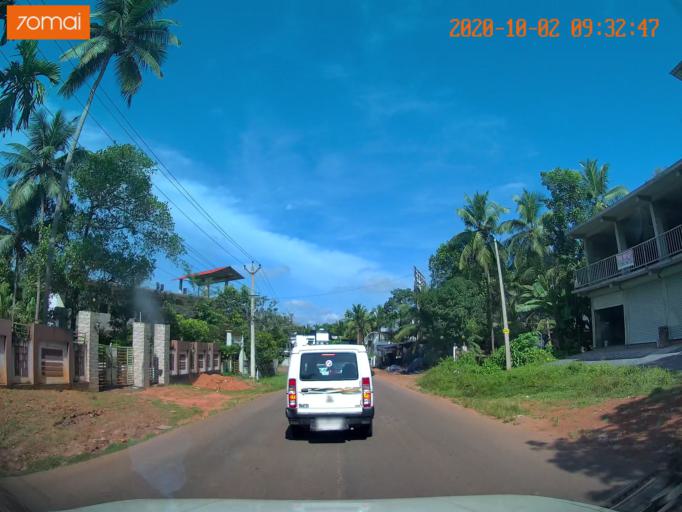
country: IN
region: Kerala
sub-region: Kozhikode
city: Nadapuram
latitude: 11.6283
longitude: 75.7544
